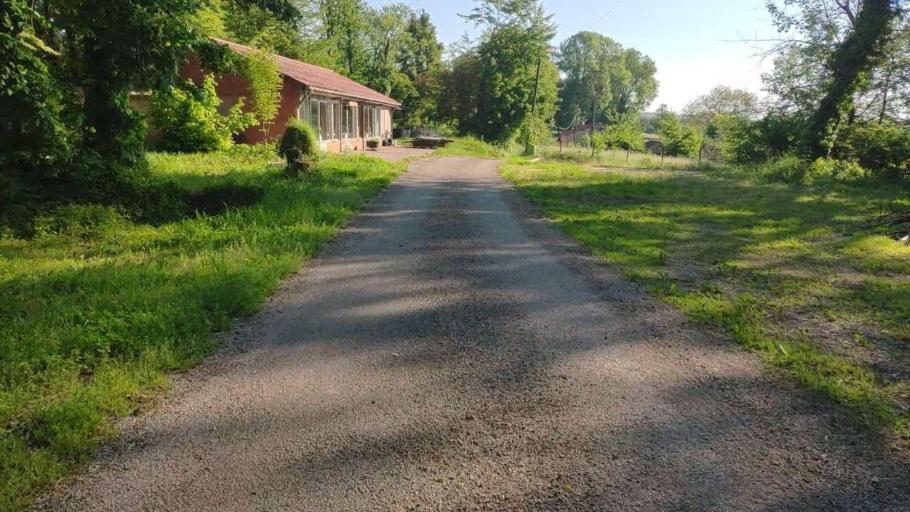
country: FR
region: Franche-Comte
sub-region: Departement du Jura
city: Perrigny
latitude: 46.7285
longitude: 5.6201
